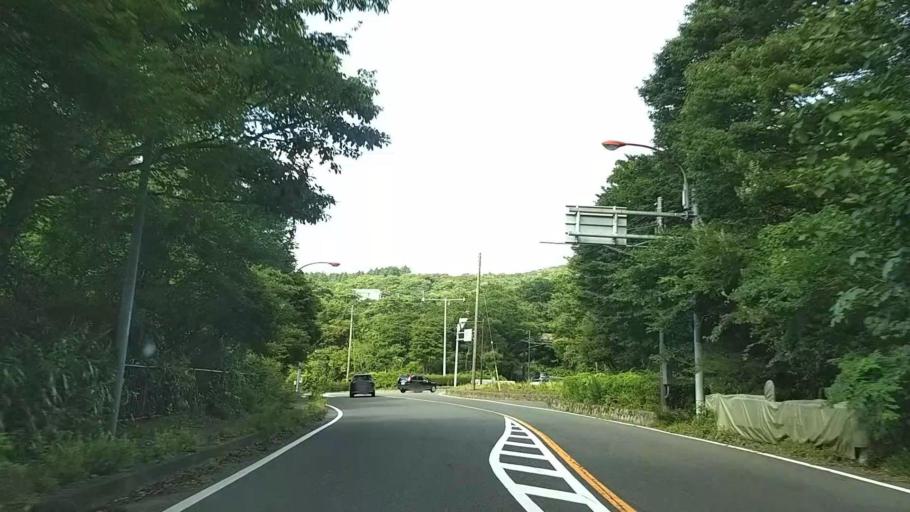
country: JP
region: Kanagawa
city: Hakone
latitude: 35.2365
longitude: 139.0018
